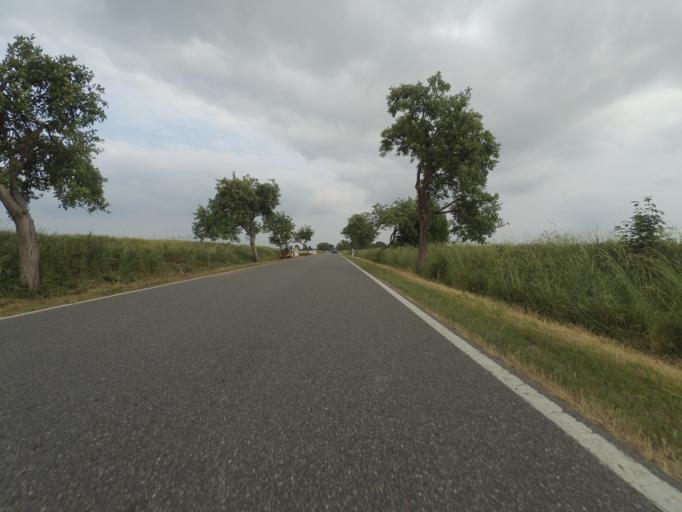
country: DE
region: Mecklenburg-Vorpommern
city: Lubz
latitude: 53.4095
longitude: 12.0924
